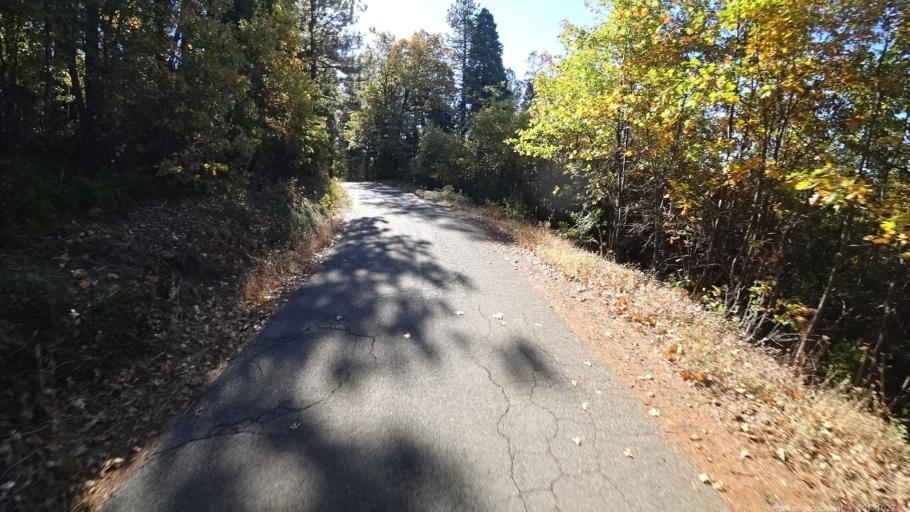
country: US
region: California
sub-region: Shasta County
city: Burney
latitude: 40.8626
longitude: -121.9231
